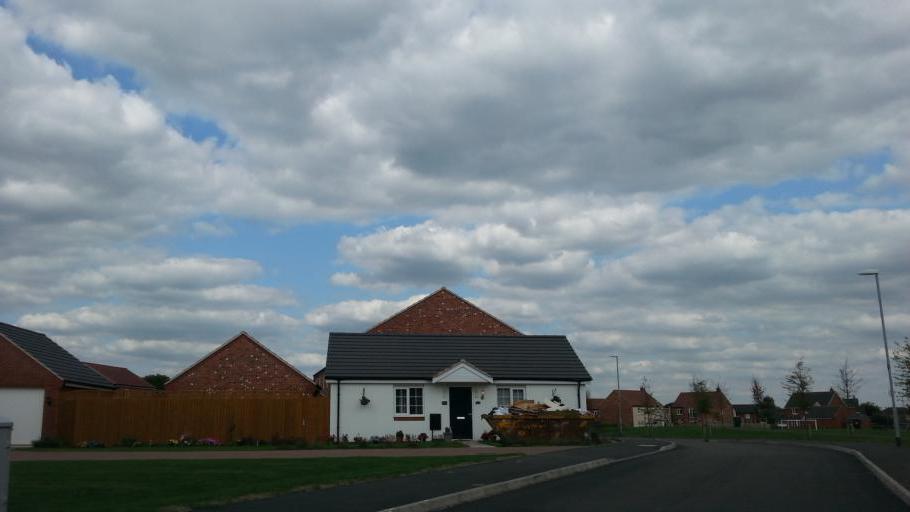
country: GB
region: England
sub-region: Leicestershire
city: Kirby Muxloe
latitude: 52.6177
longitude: -1.2322
